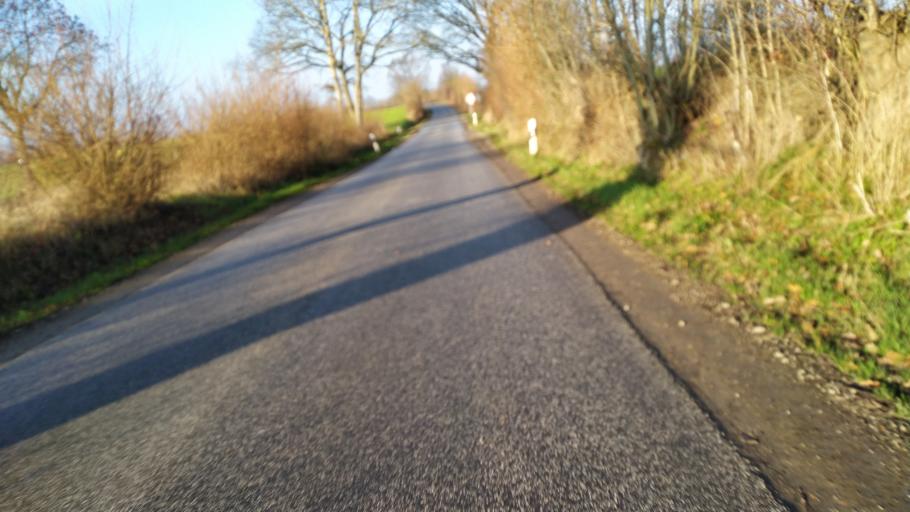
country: DE
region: Schleswig-Holstein
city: Travemuende
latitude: 53.9653
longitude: 10.8316
